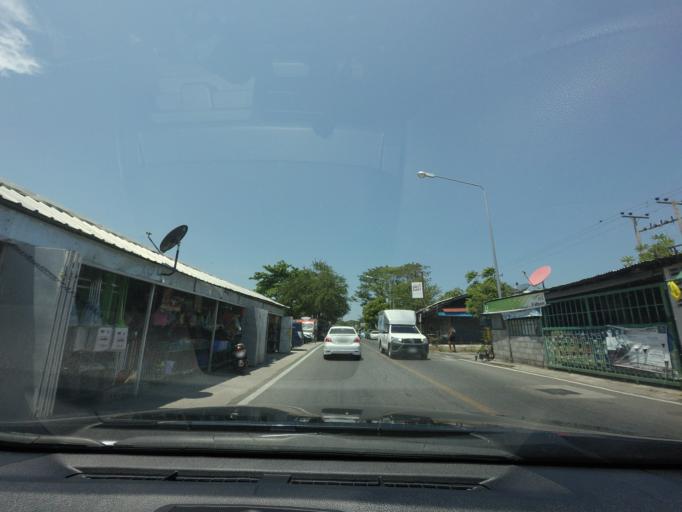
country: TH
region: Prachuap Khiri Khan
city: Hua Hin
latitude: 12.5627
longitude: 99.9559
